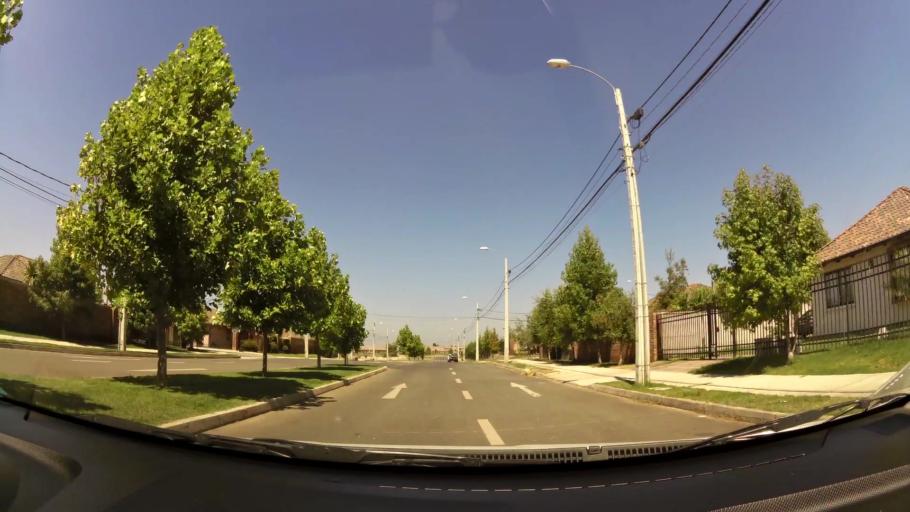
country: CL
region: Maule
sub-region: Provincia de Talca
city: Talca
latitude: -35.4319
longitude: -71.5967
